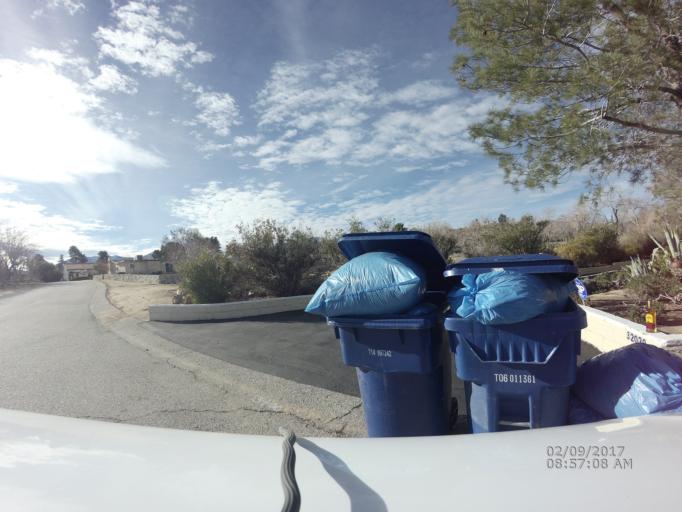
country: US
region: California
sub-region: Los Angeles County
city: Lake Los Angeles
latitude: 34.4745
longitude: -117.8426
